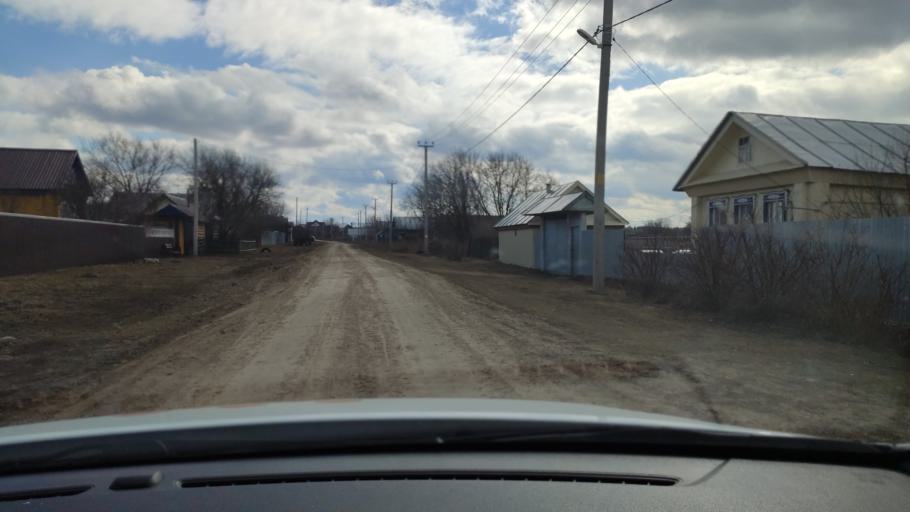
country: RU
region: Tatarstan
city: Vysokaya Gora
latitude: 56.2134
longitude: 49.3130
